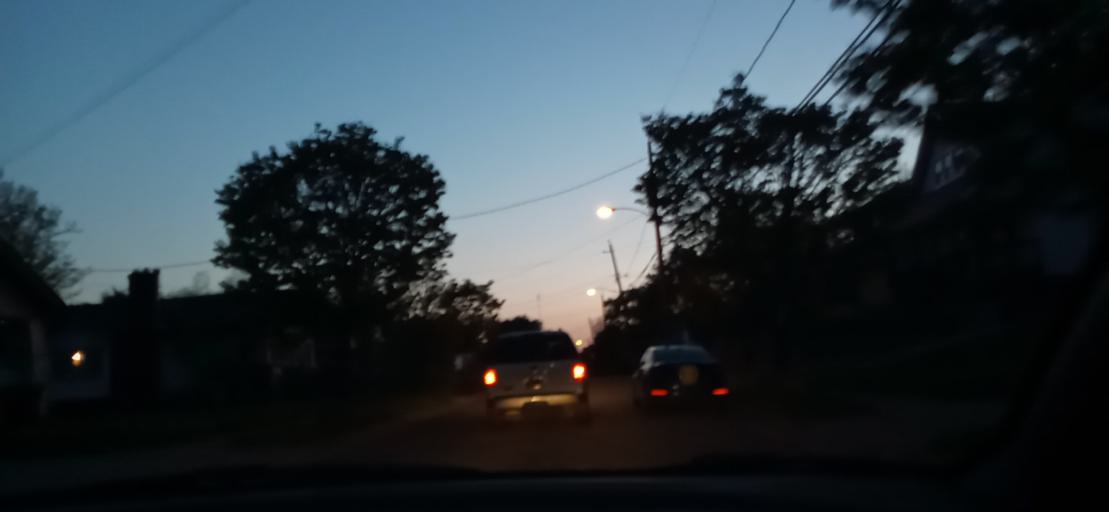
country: US
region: Ohio
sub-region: Summit County
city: Akron
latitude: 41.0647
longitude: -81.5552
